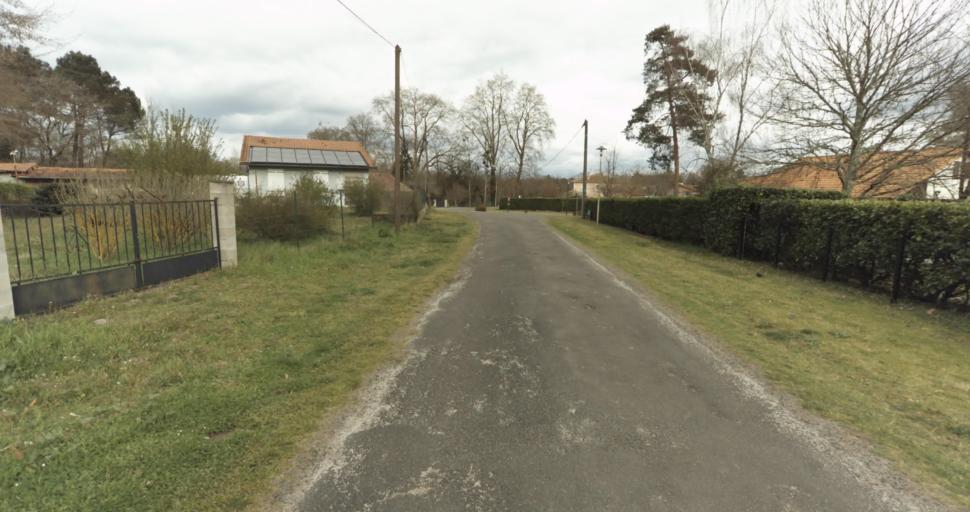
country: FR
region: Aquitaine
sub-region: Departement des Landes
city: Roquefort
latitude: 44.0417
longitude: -0.3175
